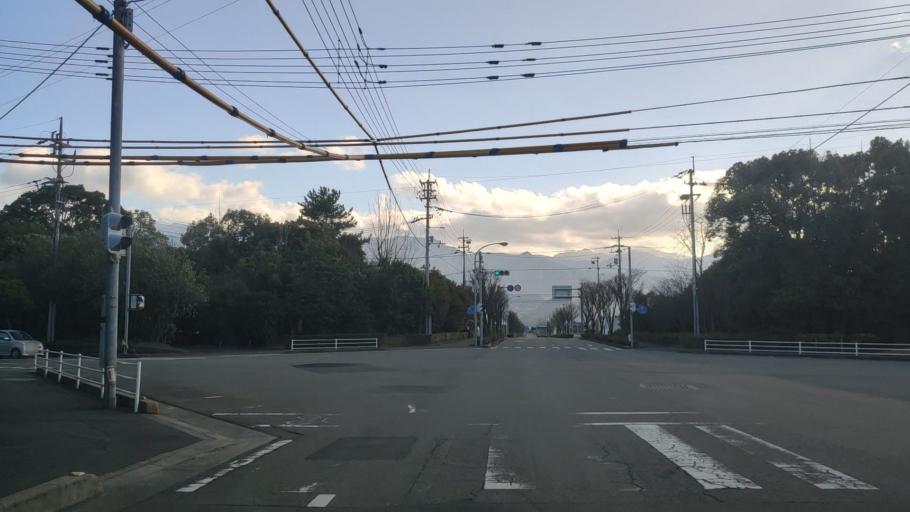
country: JP
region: Ehime
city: Saijo
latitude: 33.9355
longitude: 133.1925
